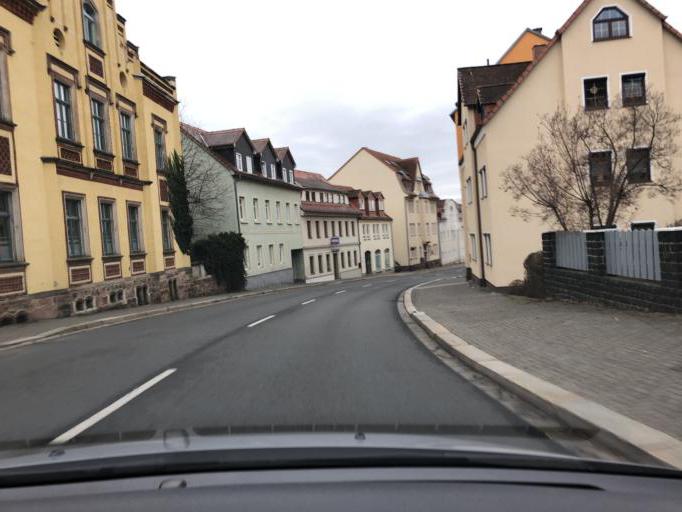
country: DE
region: Saxony
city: Dobeln
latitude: 51.1256
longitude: 13.1255
